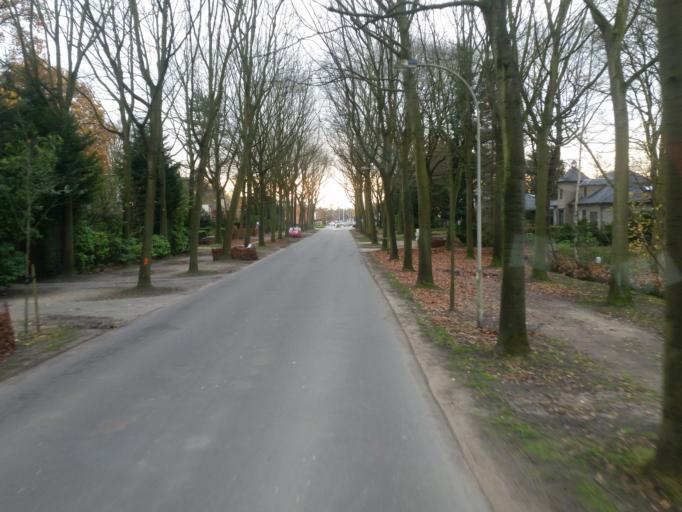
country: BE
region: Flanders
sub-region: Provincie Antwerpen
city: Brasschaat
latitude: 51.3099
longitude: 4.5052
